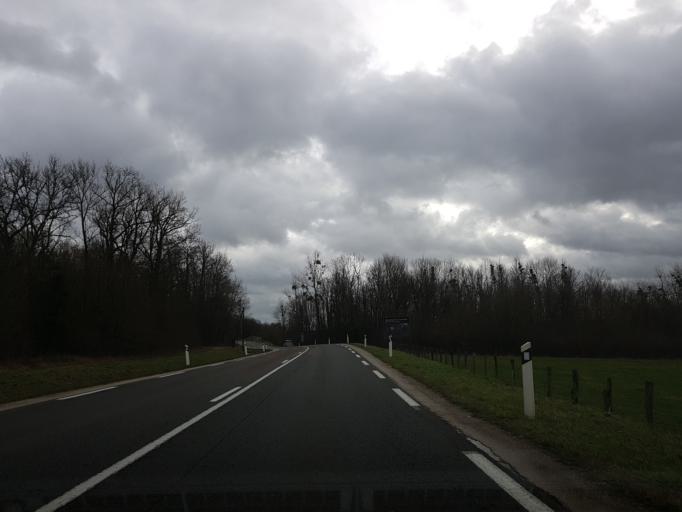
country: FR
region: Champagne-Ardenne
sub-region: Departement de la Haute-Marne
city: Chalindrey
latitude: 47.8219
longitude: 5.4822
